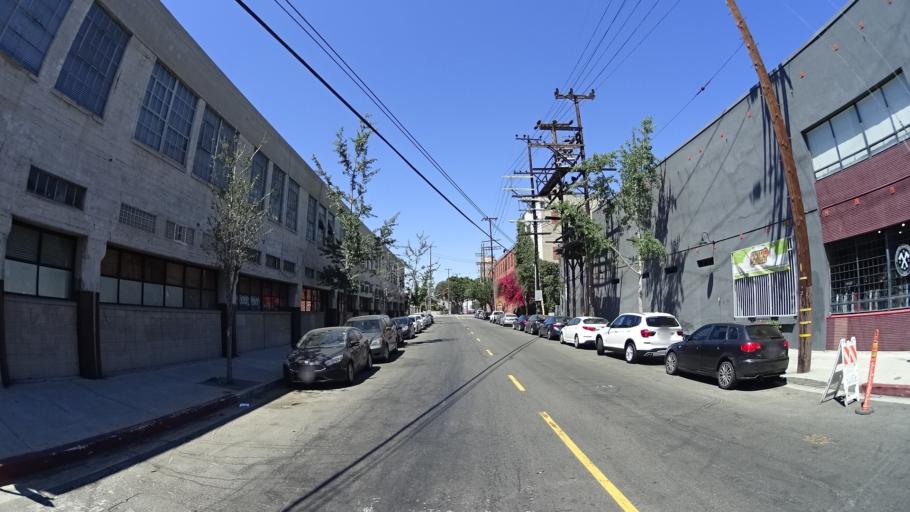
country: US
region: California
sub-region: Los Angeles County
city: Los Angeles
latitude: 34.0473
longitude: -118.2339
